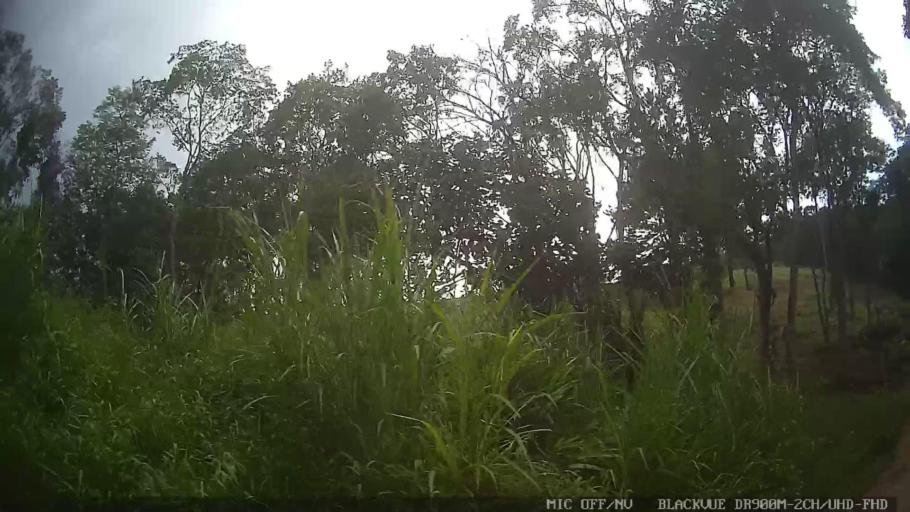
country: BR
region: Sao Paulo
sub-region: Rio Grande Da Serra
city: Rio Grande da Serra
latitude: -23.6934
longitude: -46.3245
